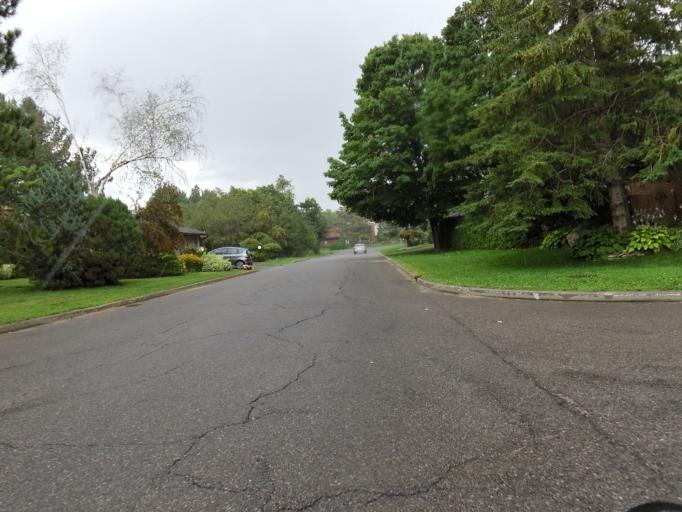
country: CA
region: Ontario
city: Bells Corners
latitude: 45.3299
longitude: -75.9101
